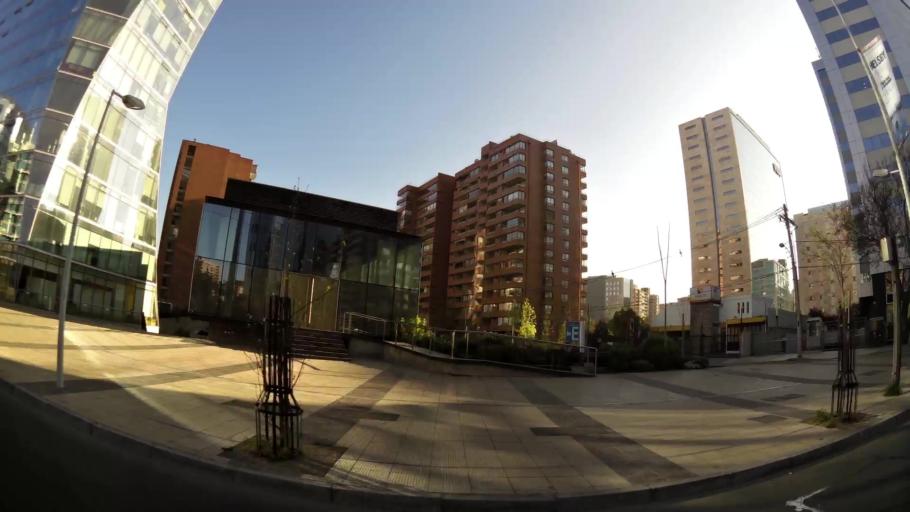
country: CL
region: Santiago Metropolitan
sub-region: Provincia de Santiago
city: Villa Presidente Frei, Nunoa, Santiago, Chile
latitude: -33.4076
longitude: -70.5698
